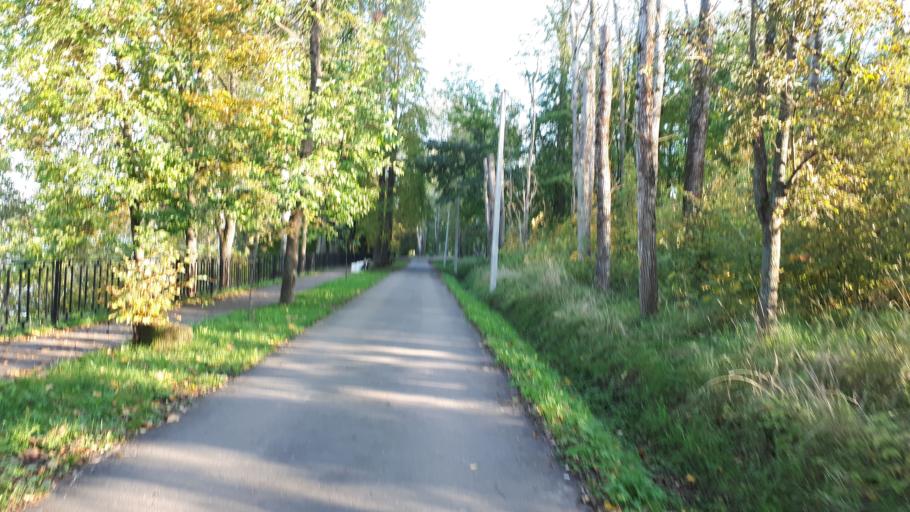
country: RU
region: Jaroslavl
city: Konstantinovskiy
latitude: 57.8305
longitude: 39.6008
